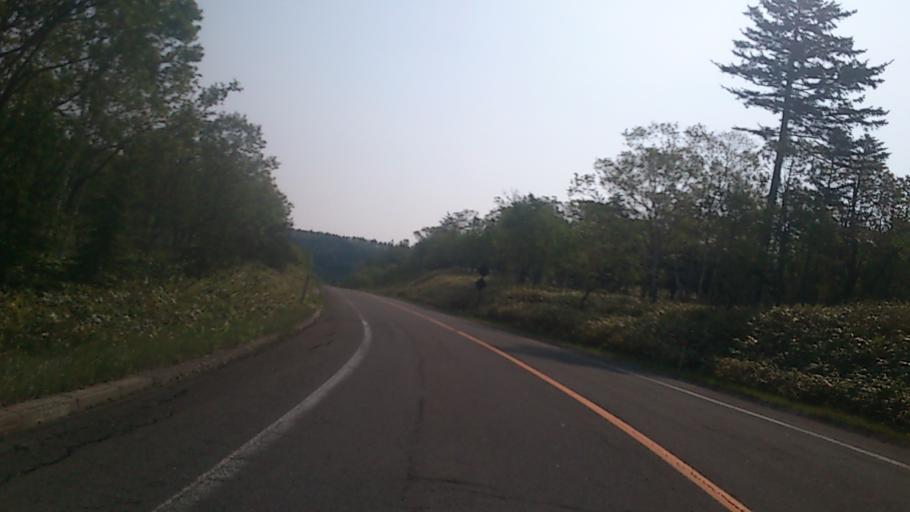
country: JP
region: Hokkaido
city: Bihoro
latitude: 43.4454
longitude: 144.2118
